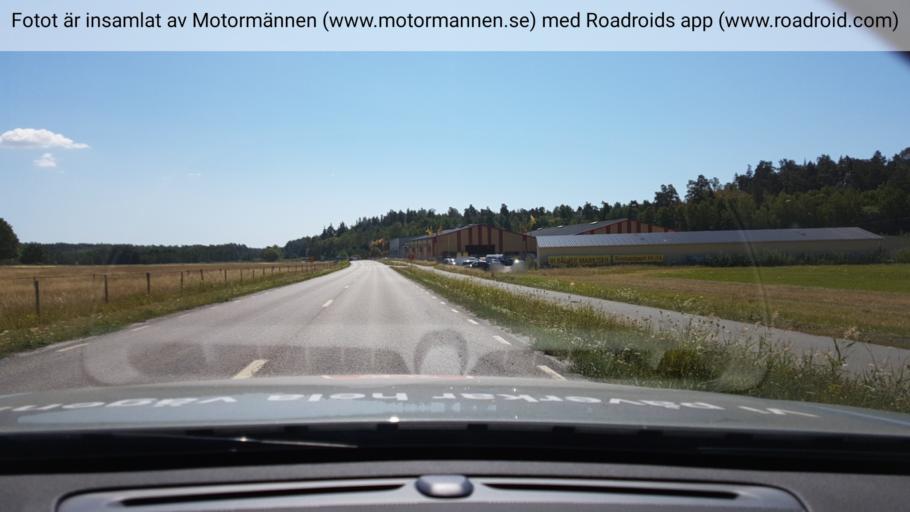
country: SE
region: Stockholm
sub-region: Ekero Kommun
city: Ekeroe
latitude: 59.3116
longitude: 17.7739
